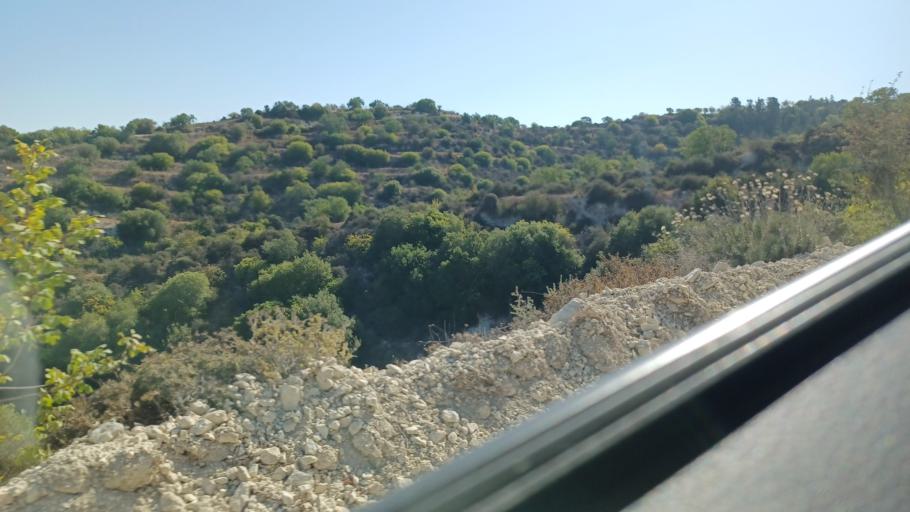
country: CY
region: Pafos
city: Tala
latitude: 34.8634
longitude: 32.4432
